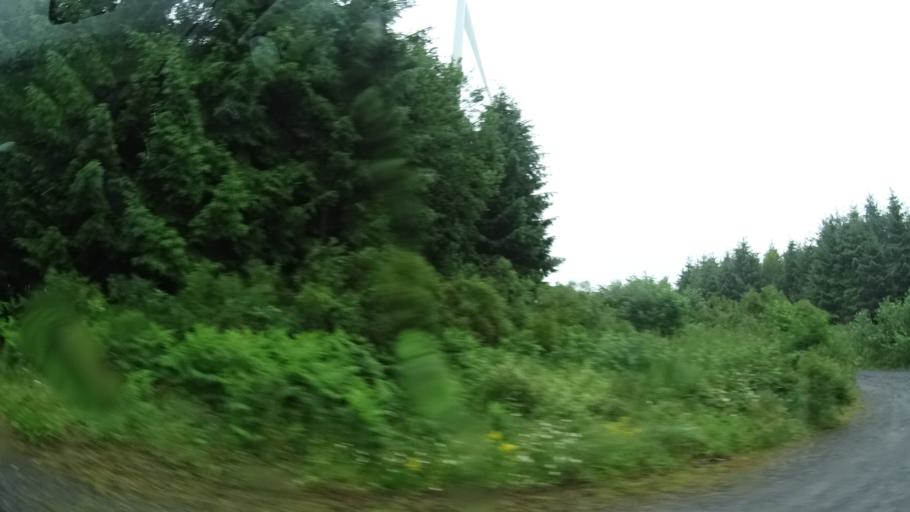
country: BE
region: Wallonia
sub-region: Province de Namur
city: Bievre
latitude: 49.9536
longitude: 5.0283
